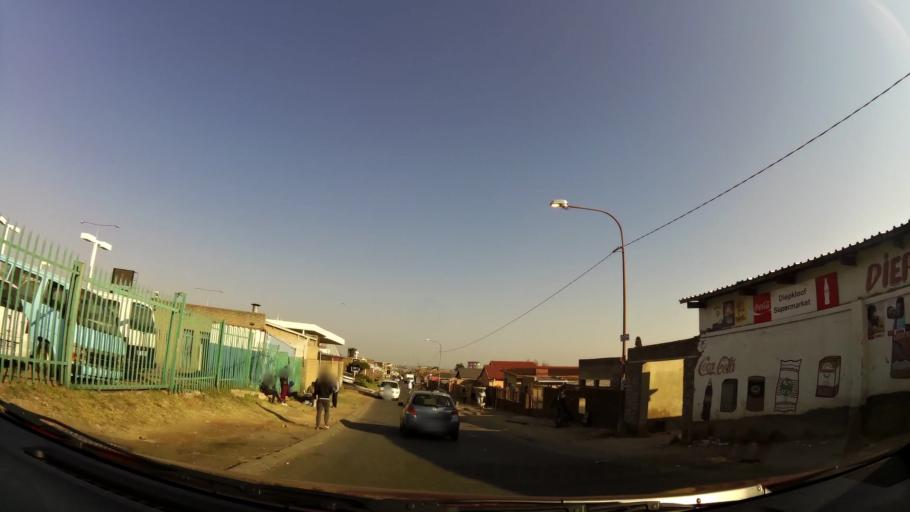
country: ZA
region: Gauteng
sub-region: City of Johannesburg Metropolitan Municipality
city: Soweto
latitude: -26.2598
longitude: 27.9477
